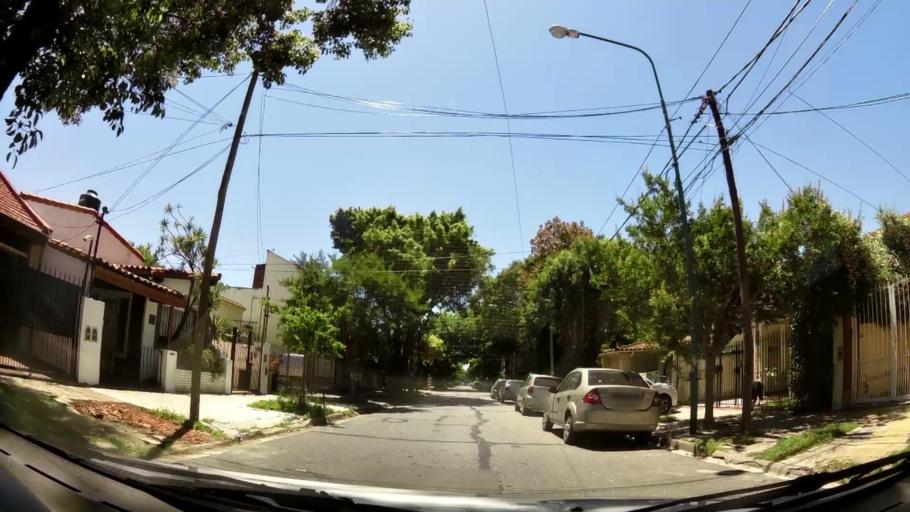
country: AR
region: Buenos Aires
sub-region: Partido de Vicente Lopez
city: Olivos
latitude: -34.5051
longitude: -58.5009
